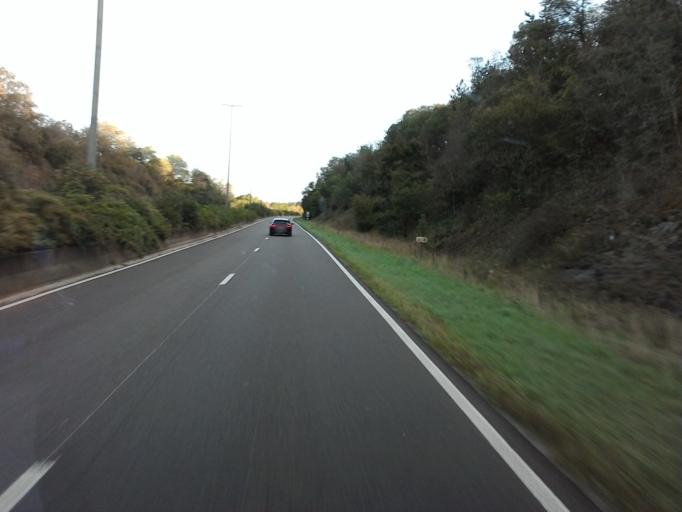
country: BE
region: Wallonia
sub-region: Province de Namur
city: Somme-Leuze
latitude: 50.3079
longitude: 5.3433
